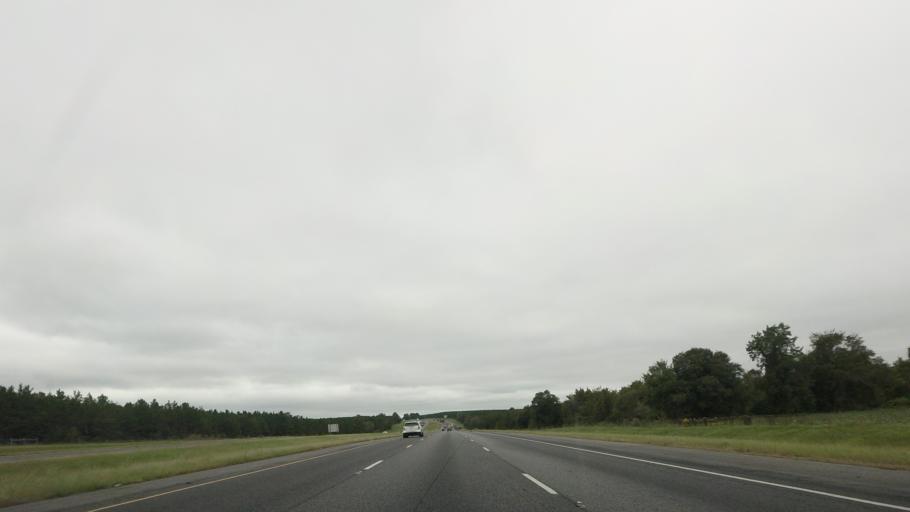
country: US
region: Georgia
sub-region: Turner County
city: Ashburn
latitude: 31.8159
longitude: -83.7090
